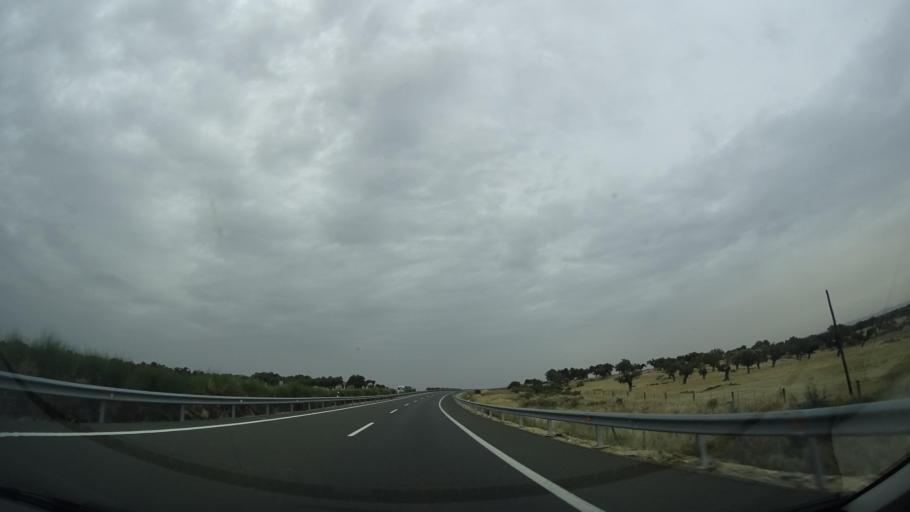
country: ES
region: Extremadura
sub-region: Provincia de Caceres
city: Jaraicejo
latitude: 39.6037
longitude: -5.8379
